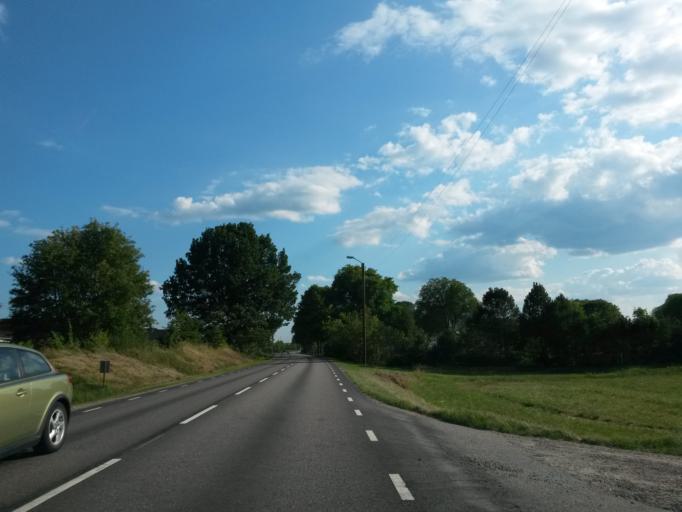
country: SE
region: Vaestra Goetaland
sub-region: Vargarda Kommun
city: Vargarda
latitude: 58.0450
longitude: 12.8146
